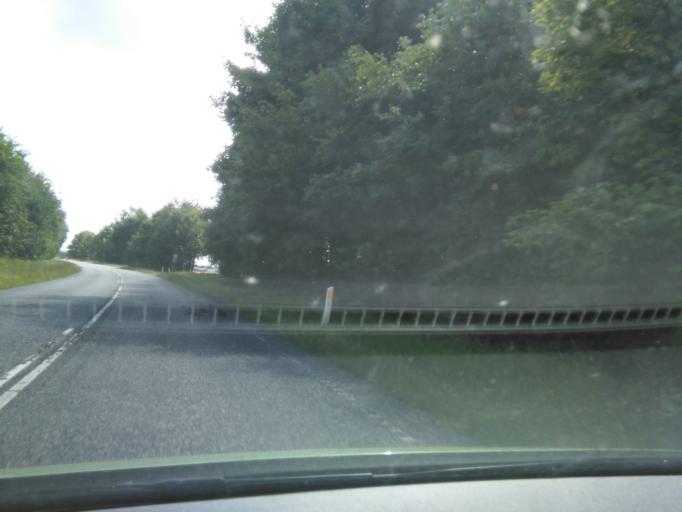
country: DK
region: Central Jutland
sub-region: Odder Kommune
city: Odder
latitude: 55.9672
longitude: 10.0807
